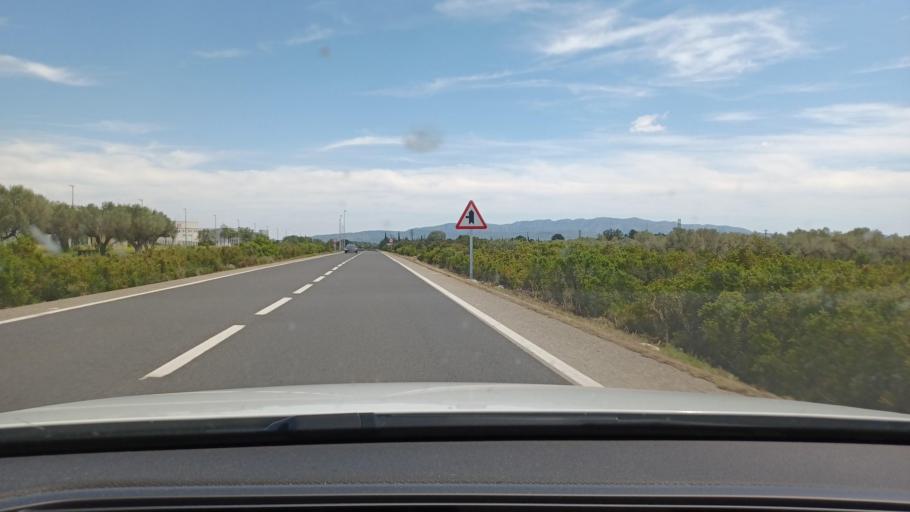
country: ES
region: Catalonia
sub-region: Provincia de Tarragona
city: Mas de Barberans
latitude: 40.6386
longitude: 0.3335
